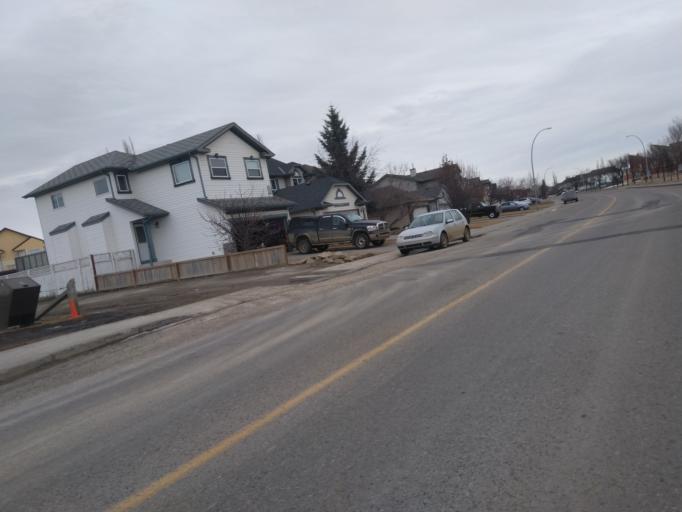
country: CA
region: Alberta
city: Calgary
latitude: 51.1648
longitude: -114.0480
